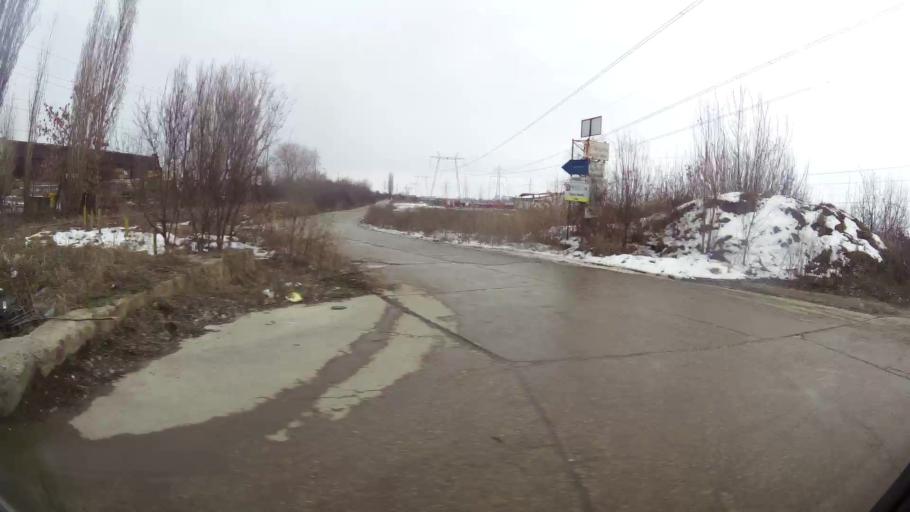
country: RO
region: Ilfov
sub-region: Comuna Glina
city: Catelu
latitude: 44.3981
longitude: 26.2019
